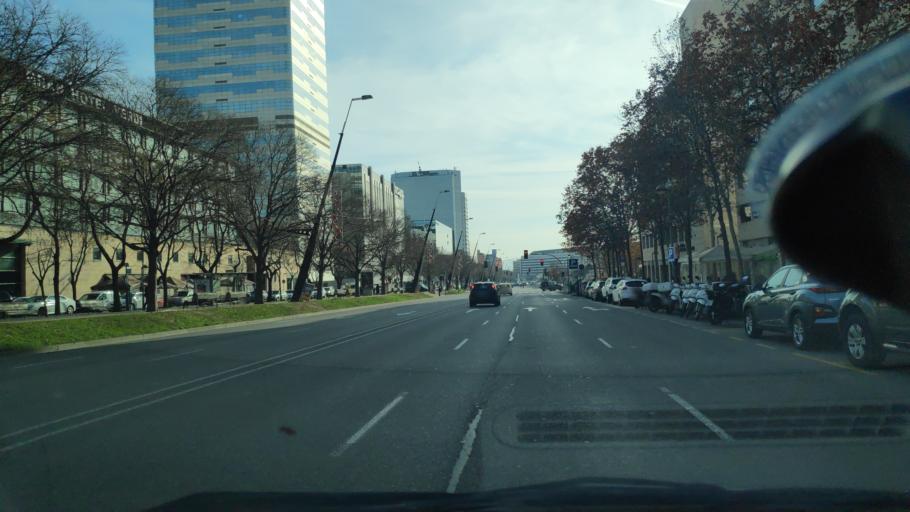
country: ES
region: Catalonia
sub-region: Provincia de Barcelona
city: Sabadell
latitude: 41.5563
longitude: 2.0973
